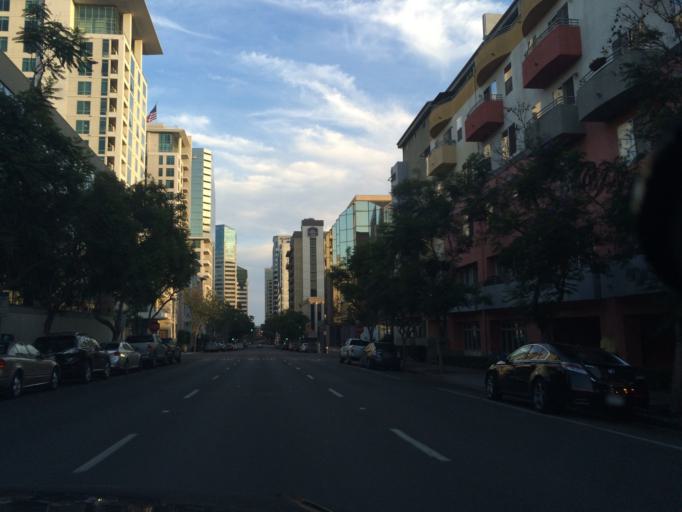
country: US
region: California
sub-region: San Diego County
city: San Diego
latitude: 32.7215
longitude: -117.1674
